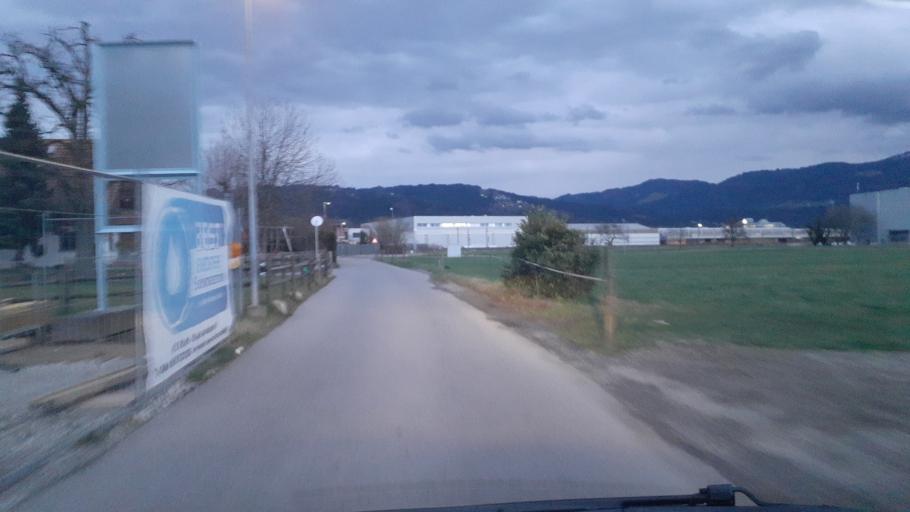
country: AT
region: Vorarlberg
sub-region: Politischer Bezirk Bregenz
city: Lauterach
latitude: 47.4706
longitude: 9.7220
